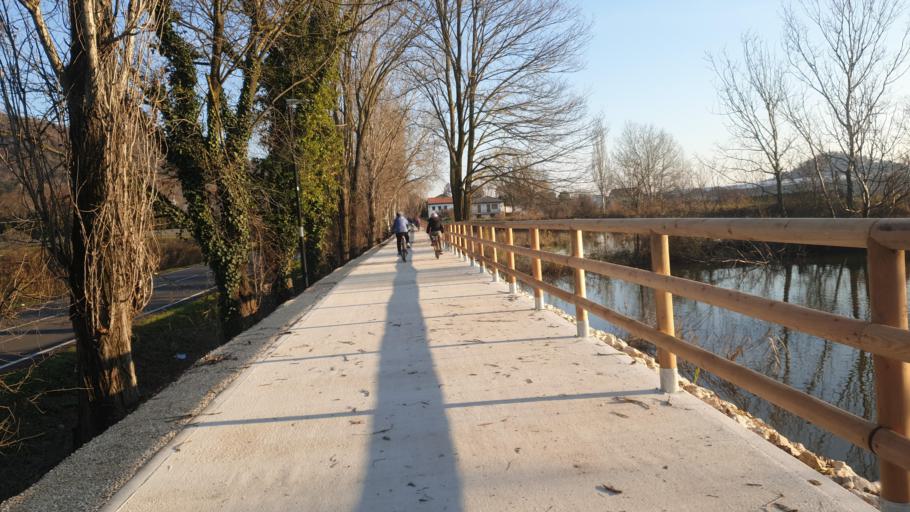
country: IT
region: Veneto
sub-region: Provincia di Padova
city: Galzignano
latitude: 45.3013
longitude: 11.7519
